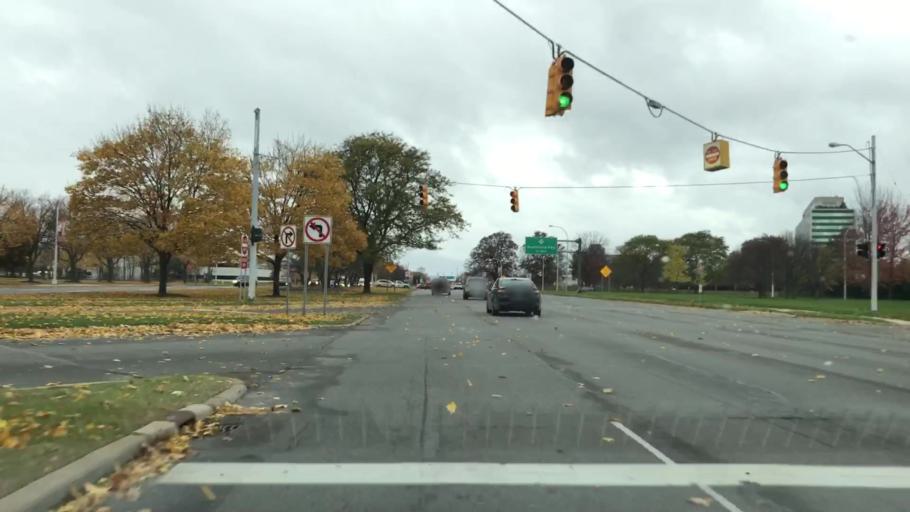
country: US
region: Michigan
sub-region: Wayne County
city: Dearborn
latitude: 42.3144
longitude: -83.2024
